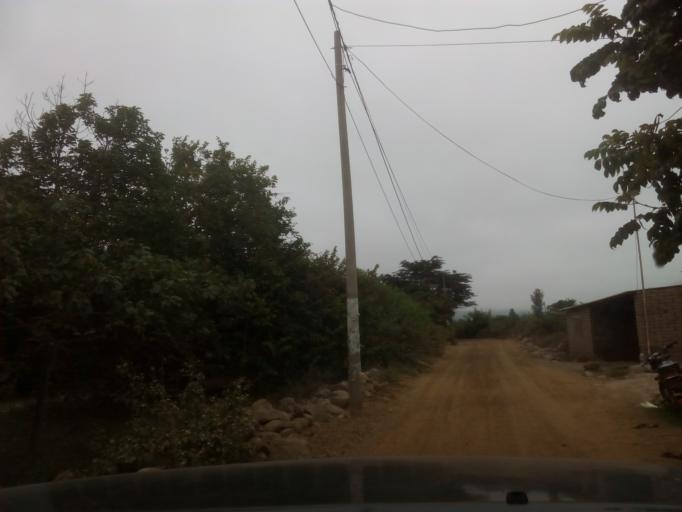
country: PE
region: La Libertad
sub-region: Viru
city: Viru
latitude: -8.3749
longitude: -78.6521
